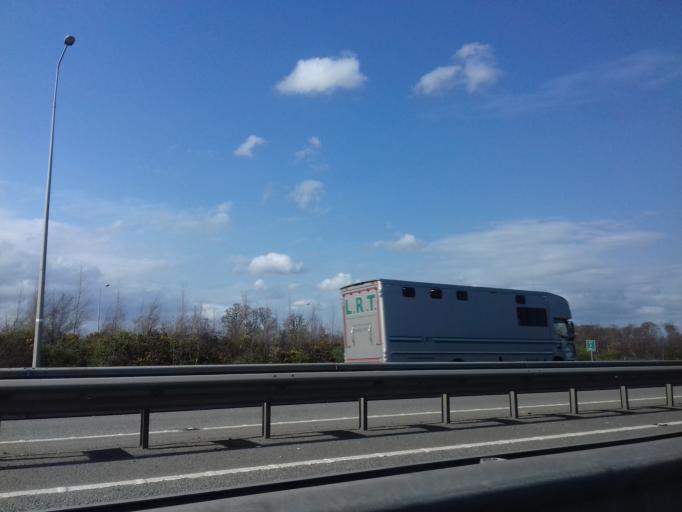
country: IE
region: Leinster
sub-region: Kildare
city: Johnstown
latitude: 53.2381
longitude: -6.6183
